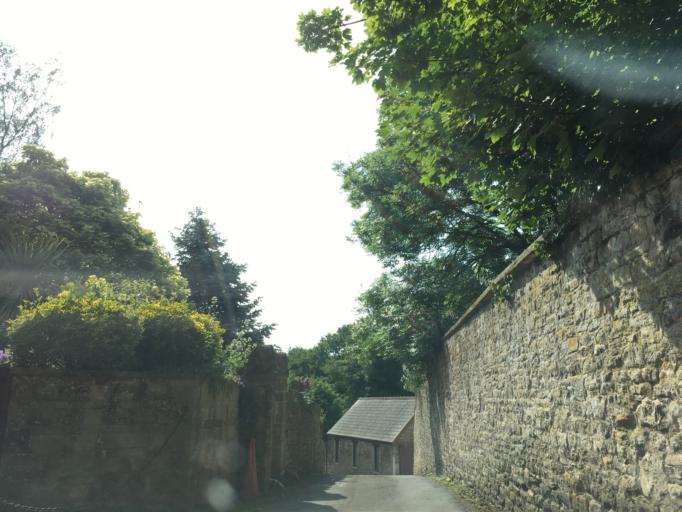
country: GB
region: England
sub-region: Gloucestershire
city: Brimscombe
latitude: 51.7223
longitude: -2.1927
